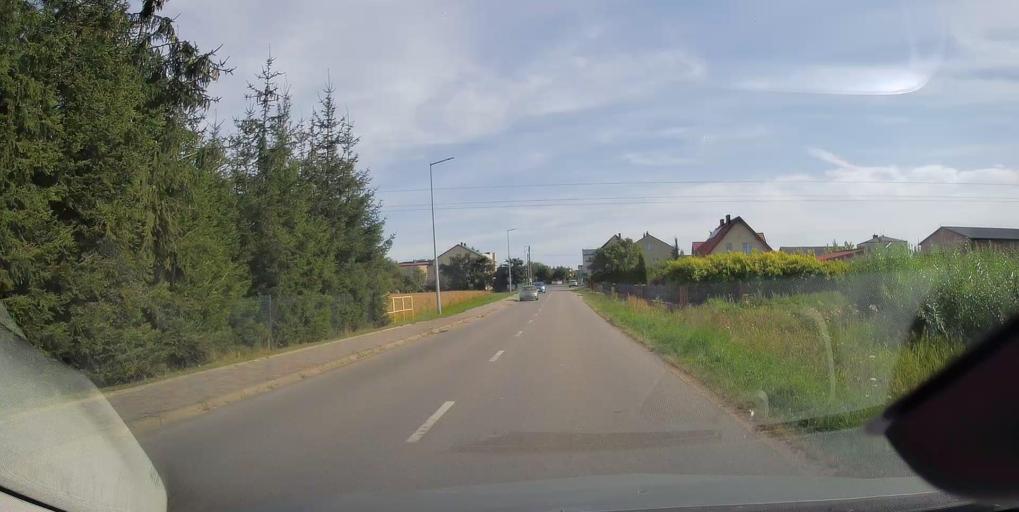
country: PL
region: Lodz Voivodeship
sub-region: Powiat opoczynski
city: Mniszkow
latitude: 51.3719
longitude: 20.0390
